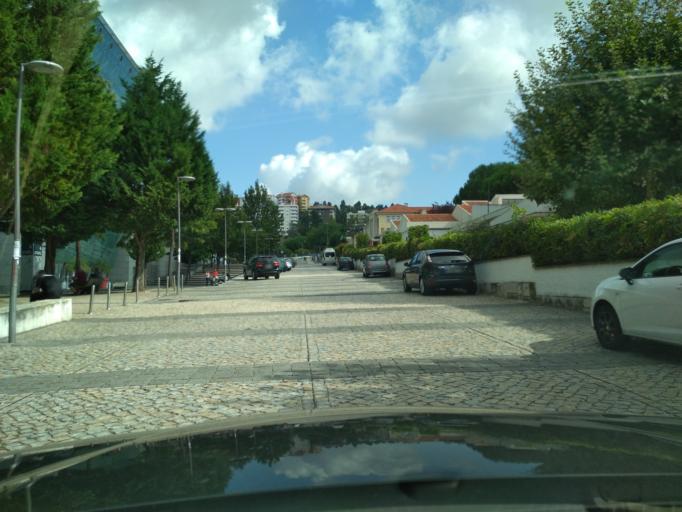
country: PT
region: Coimbra
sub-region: Coimbra
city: Coimbra
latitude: 40.2036
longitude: -8.4064
